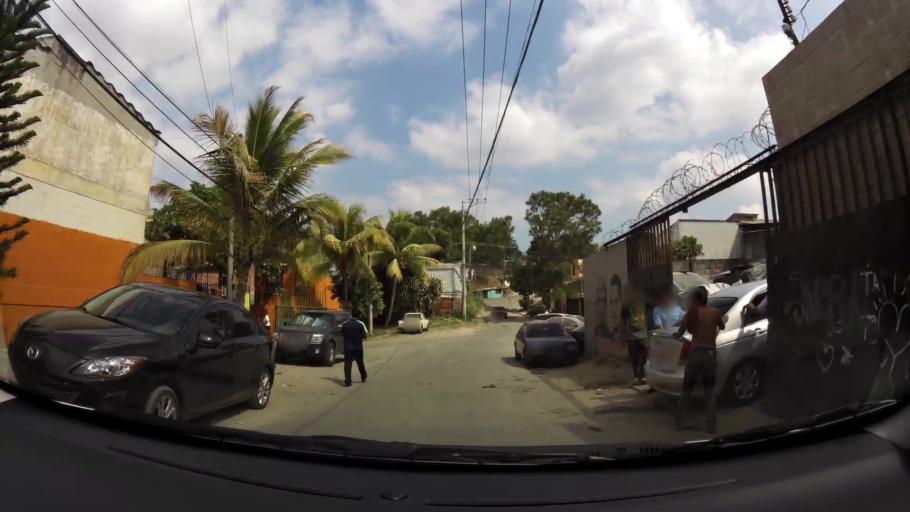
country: SV
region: San Salvador
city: Mejicanos
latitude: 13.7165
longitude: -89.2330
